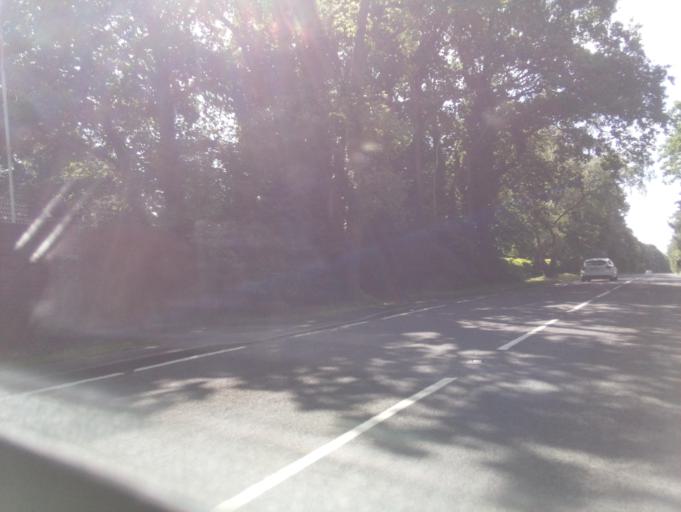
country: GB
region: England
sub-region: North Lincolnshire
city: Manton
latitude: 53.5303
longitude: -0.5775
